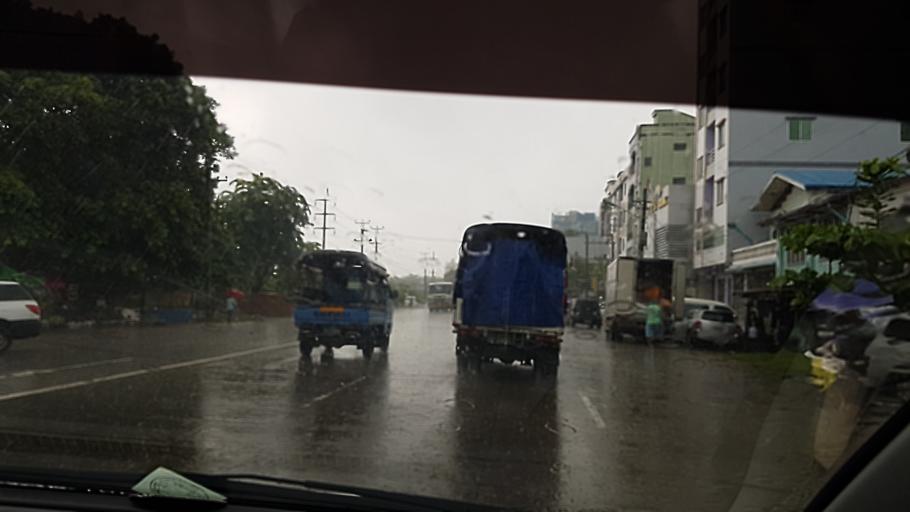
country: MM
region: Yangon
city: Yangon
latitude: 16.7800
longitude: 96.1910
